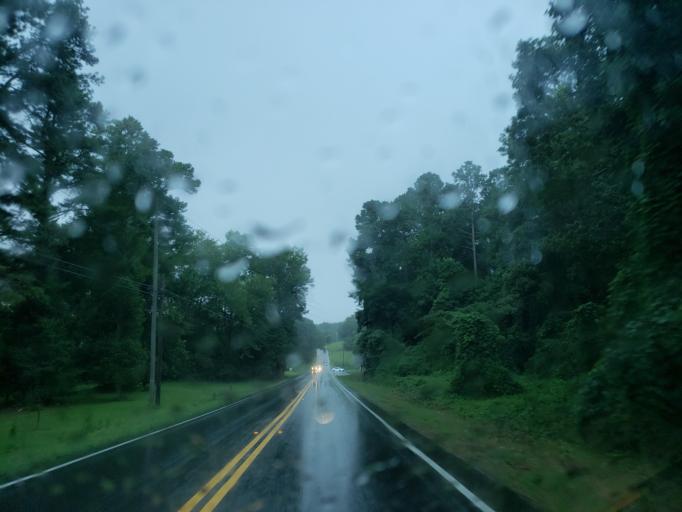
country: US
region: Georgia
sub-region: Cherokee County
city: Canton
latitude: 34.3104
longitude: -84.4616
